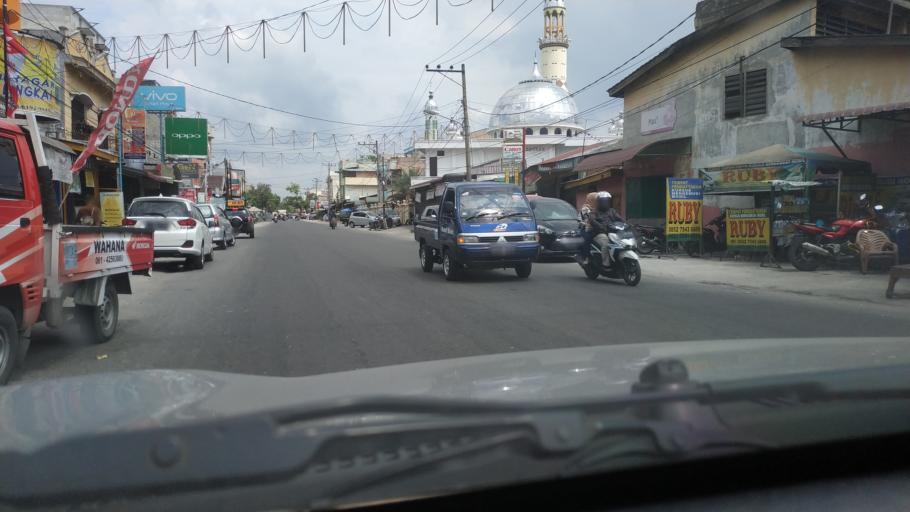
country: ID
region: North Sumatra
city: Sunggal
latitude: 3.5854
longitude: 98.6142
